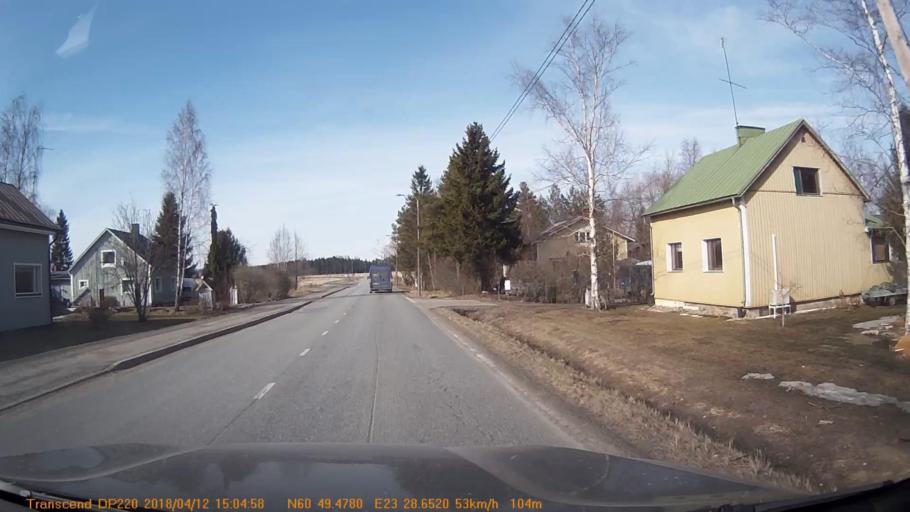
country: FI
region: Haeme
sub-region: Forssa
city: Jokioinen
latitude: 60.8248
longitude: 23.4775
